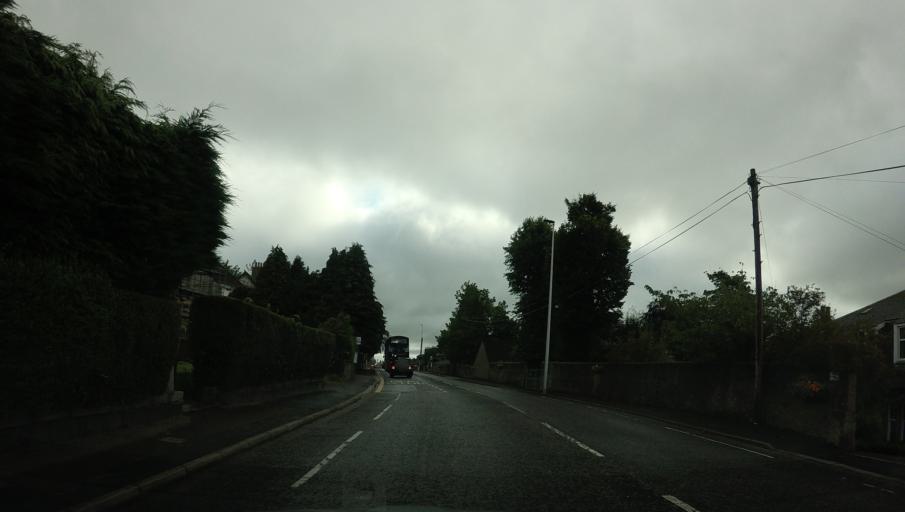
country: GB
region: Scotland
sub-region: Aberdeenshire
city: Westhill
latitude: 57.0963
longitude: -2.2611
